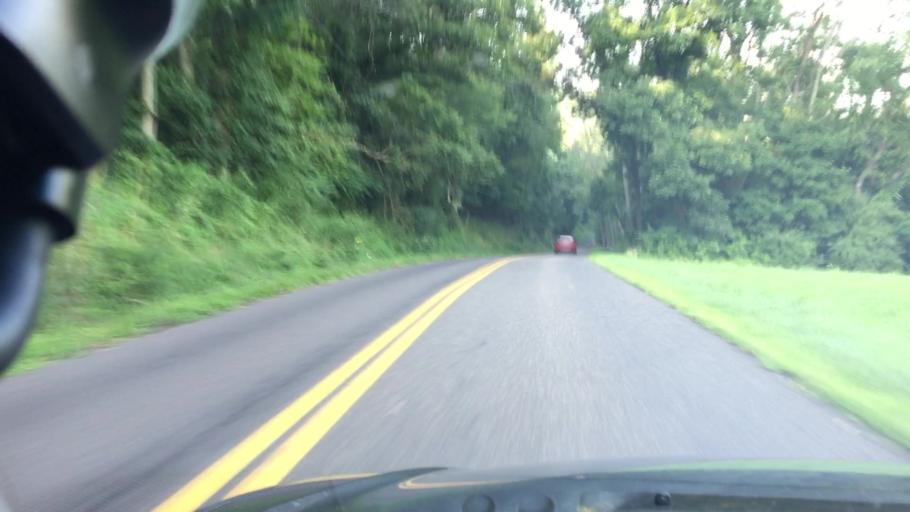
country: US
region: Pennsylvania
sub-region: Columbia County
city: Catawissa
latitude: 40.9590
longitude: -76.4441
